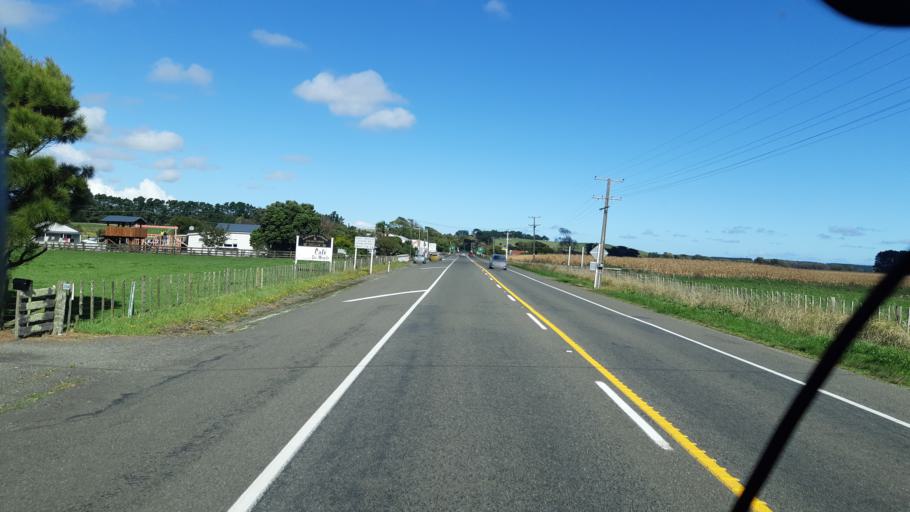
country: NZ
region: Manawatu-Wanganui
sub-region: Wanganui District
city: Wanganui
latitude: -40.0370
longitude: 175.2121
